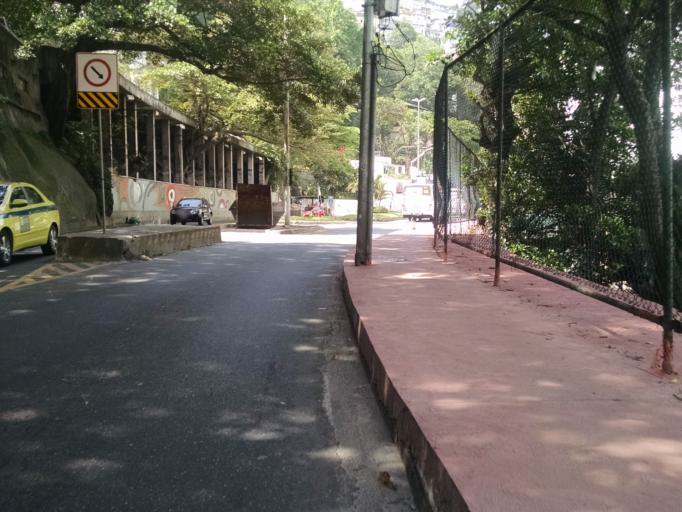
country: BR
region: Rio de Janeiro
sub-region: Rio De Janeiro
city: Rio de Janeiro
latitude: -22.9927
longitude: -43.2339
